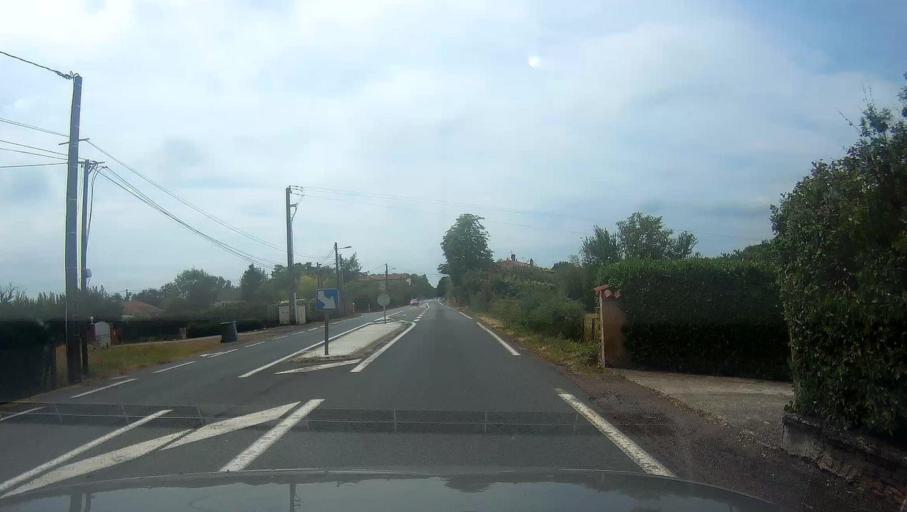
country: FR
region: Rhone-Alpes
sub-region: Departement du Rhone
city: Theize
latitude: 45.9336
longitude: 4.6526
